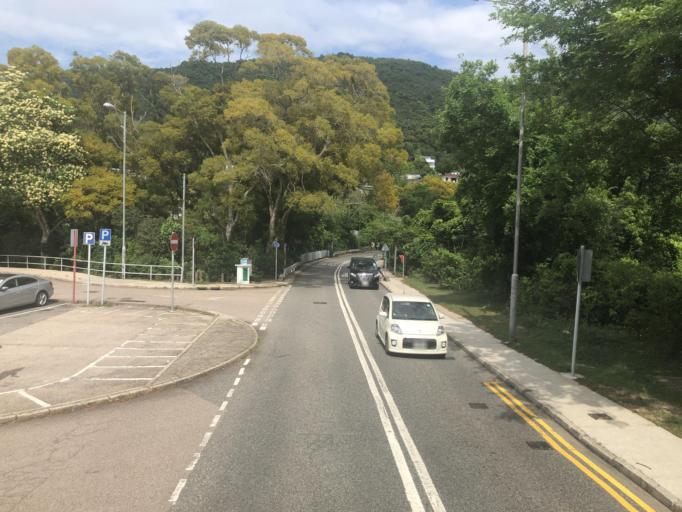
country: HK
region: Sai Kung
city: Sai Kung
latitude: 22.3921
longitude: 114.2987
